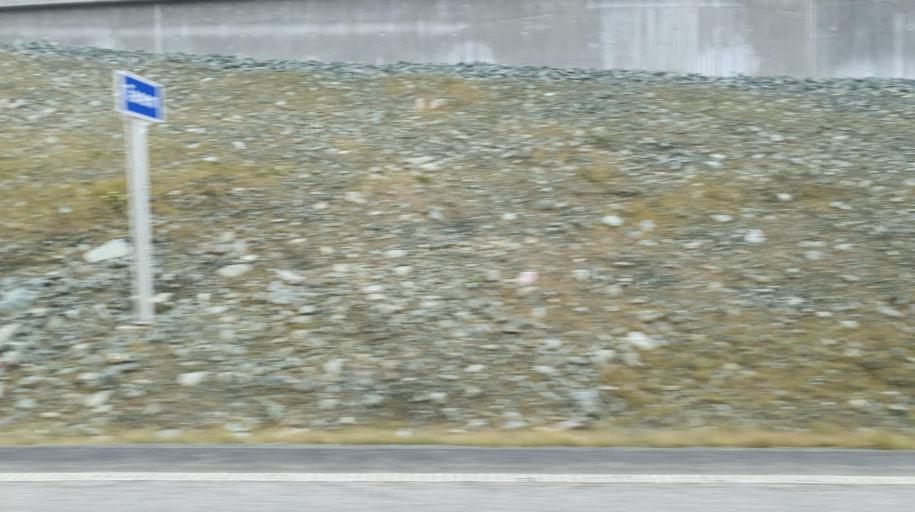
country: NO
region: Sor-Trondelag
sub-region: Klaebu
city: Klaebu
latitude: 63.3143
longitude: 10.4214
